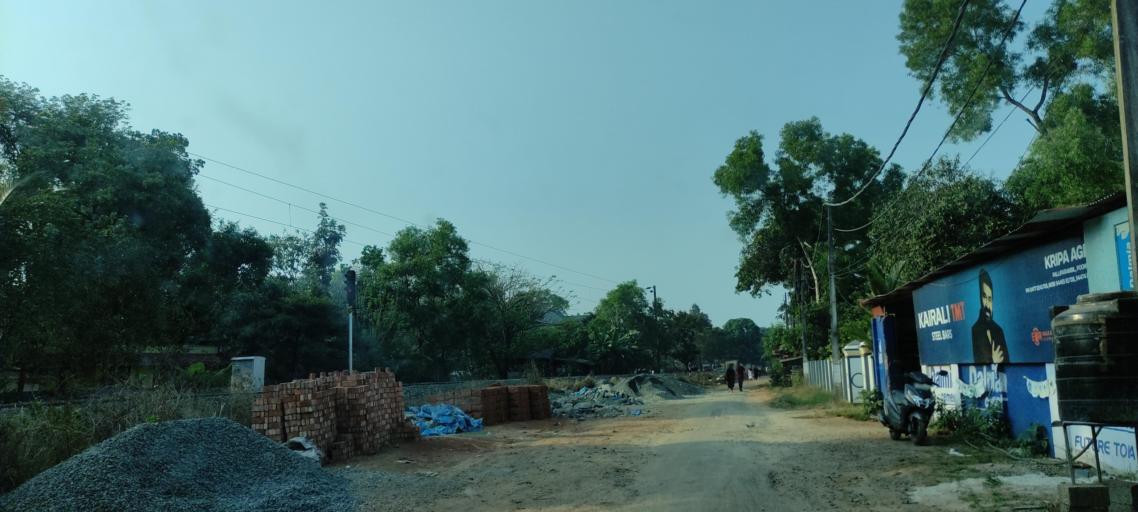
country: IN
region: Kerala
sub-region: Alappuzha
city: Alleppey
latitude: 9.5268
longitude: 76.3216
